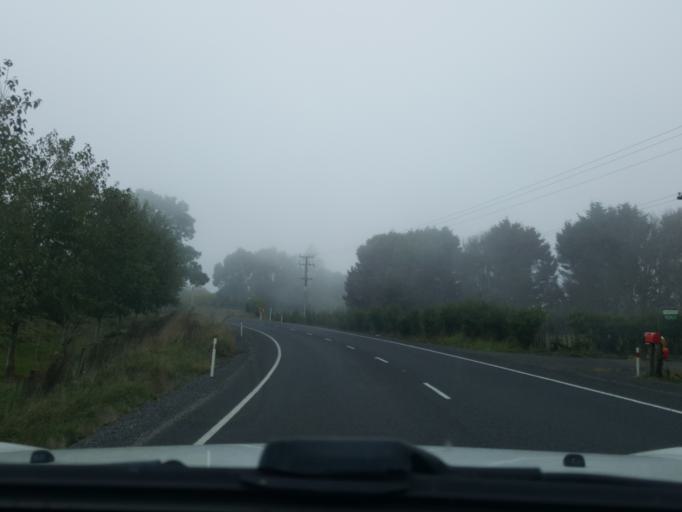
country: NZ
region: Auckland
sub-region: Auckland
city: Pukekohe East
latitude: -37.3003
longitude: 175.0308
